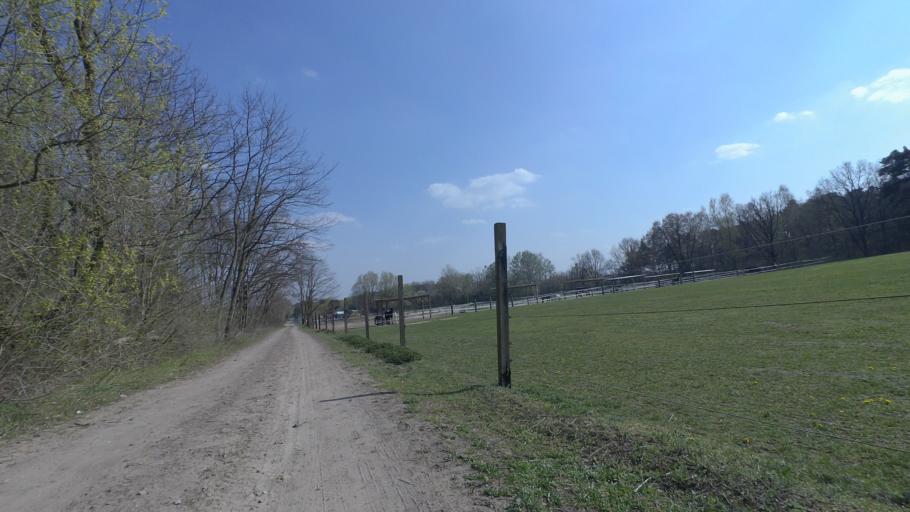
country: DE
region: Brandenburg
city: Teupitz
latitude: 52.1792
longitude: 13.5603
